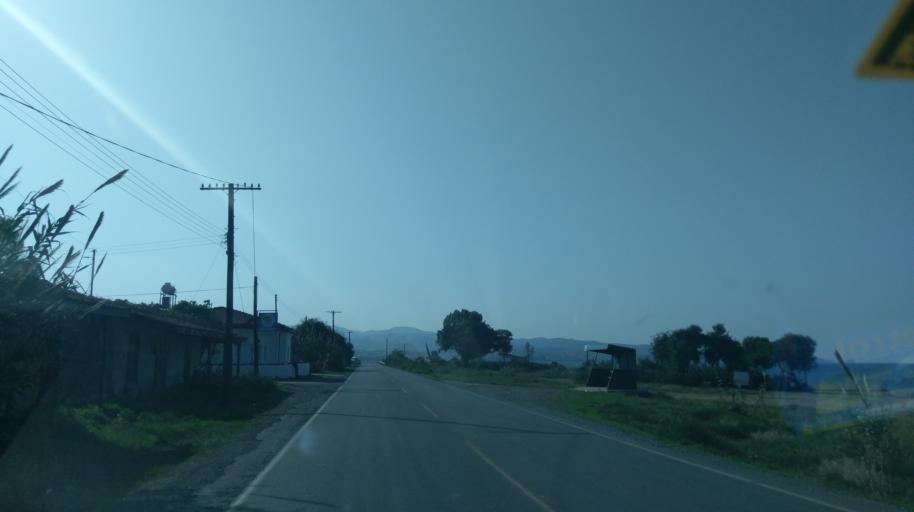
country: CY
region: Lefkosia
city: Lefka
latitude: 35.1475
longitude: 32.8504
